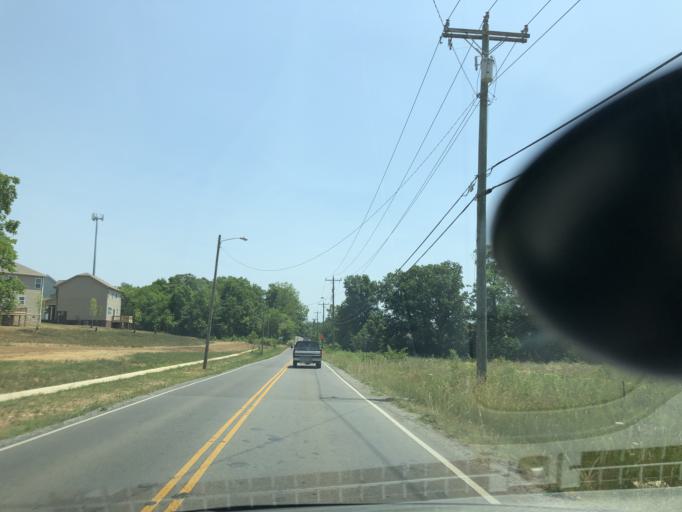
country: US
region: Tennessee
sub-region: Rutherford County
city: La Vergne
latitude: 36.0611
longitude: -86.6119
